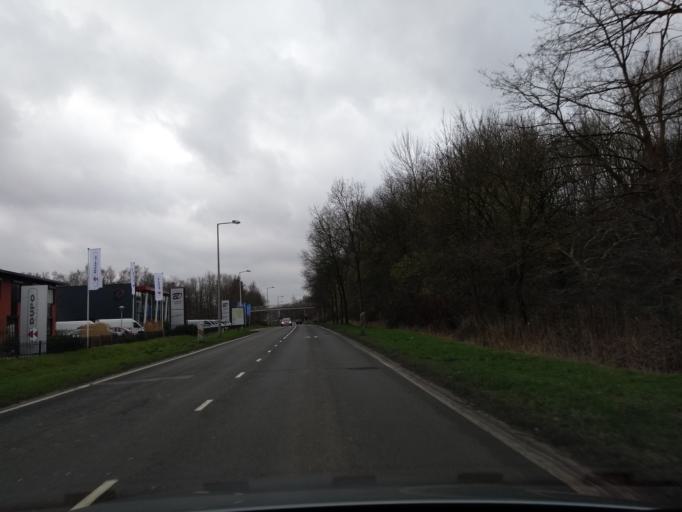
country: NL
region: Overijssel
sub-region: Gemeente Enschede
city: Enschede
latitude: 52.2241
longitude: 6.9407
